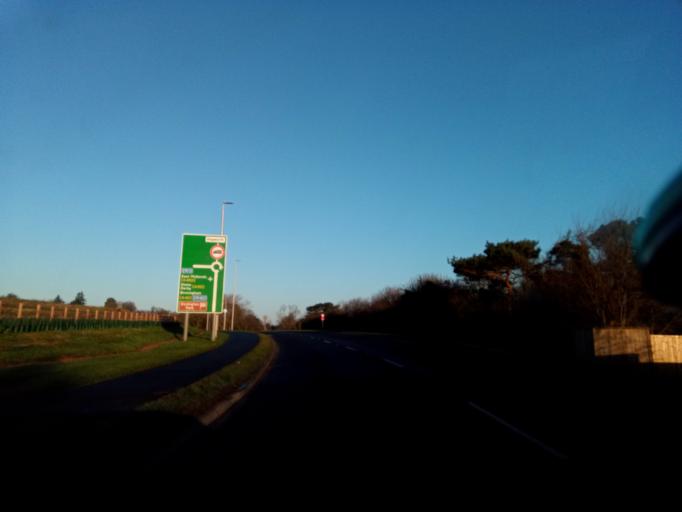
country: GB
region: England
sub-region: Leicestershire
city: Kegworth
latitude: 52.8289
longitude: -1.2738
